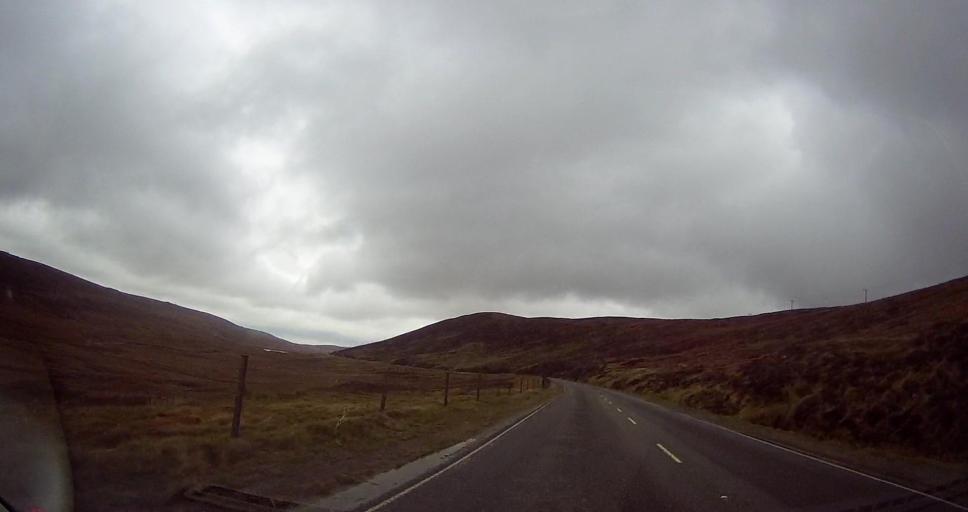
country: GB
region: Scotland
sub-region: Shetland Islands
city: Lerwick
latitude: 60.2997
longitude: -1.2391
